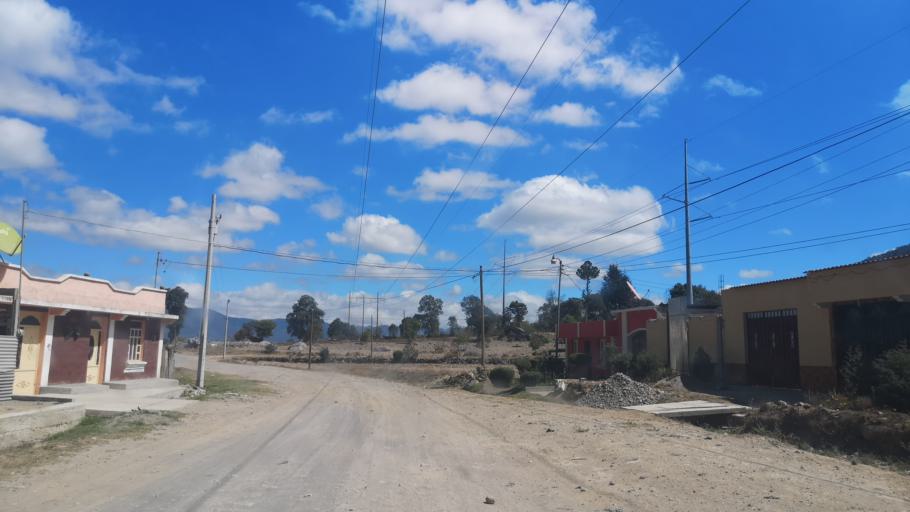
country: GT
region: Quetzaltenango
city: Quetzaltenango
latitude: 14.7991
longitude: -91.5376
